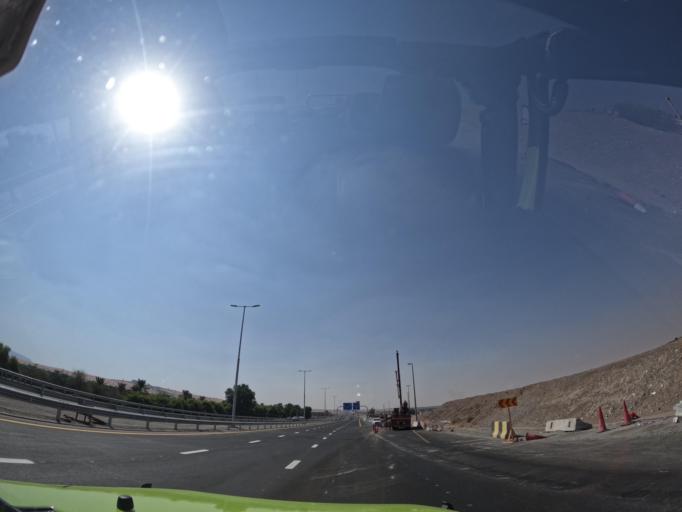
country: AE
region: Ash Shariqah
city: Adh Dhayd
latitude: 24.7785
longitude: 55.8139
